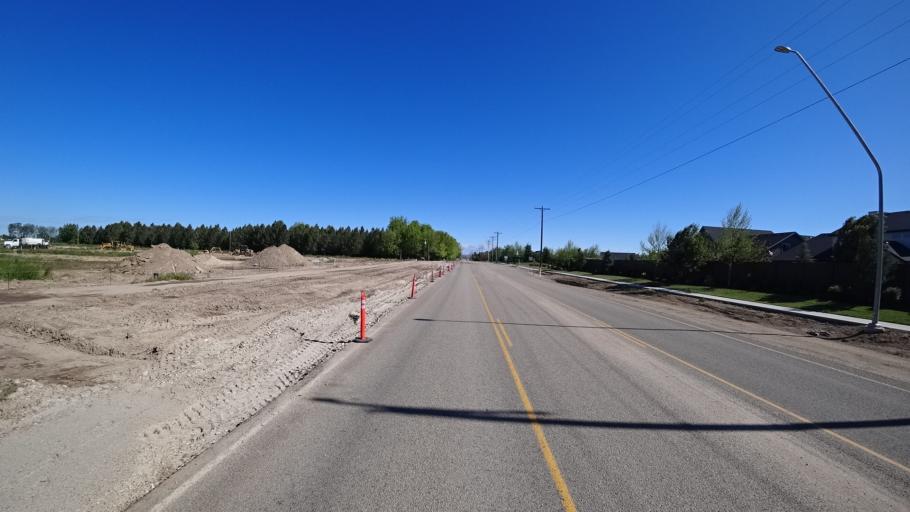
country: US
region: Idaho
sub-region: Ada County
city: Star
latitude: 43.6570
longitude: -116.4536
